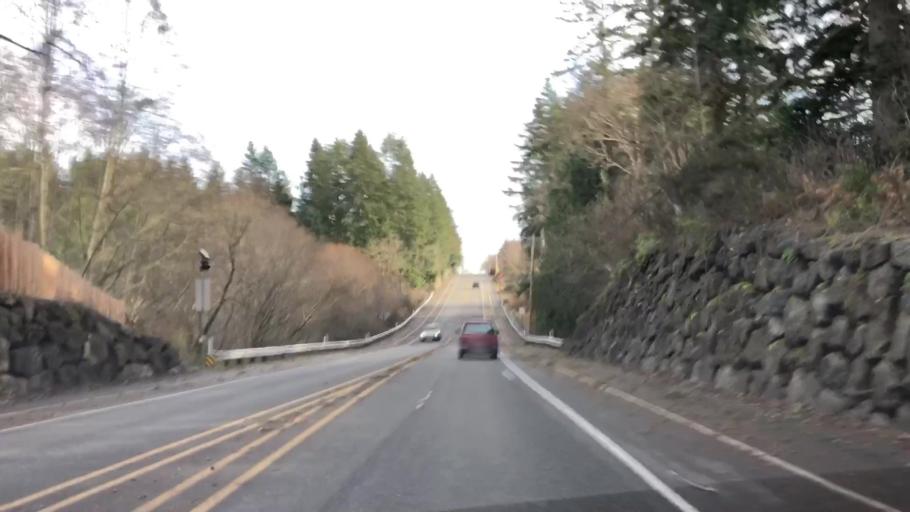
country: US
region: Washington
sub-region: Kitsap County
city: Kingston
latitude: 47.7949
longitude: -122.5234
